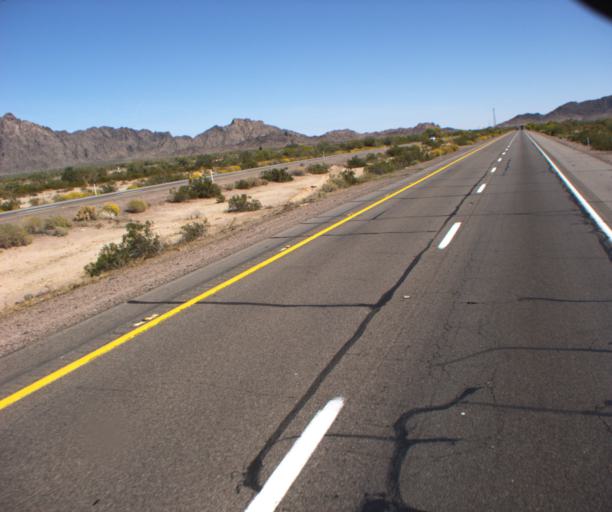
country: US
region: Arizona
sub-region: Yuma County
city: Wellton
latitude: 32.7183
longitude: -113.7887
